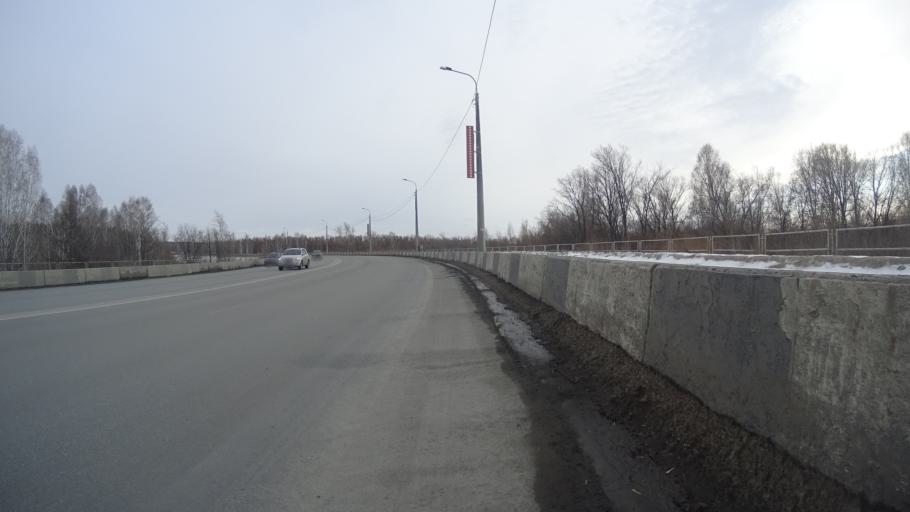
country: RU
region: Chelyabinsk
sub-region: Gorod Chelyabinsk
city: Chelyabinsk
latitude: 55.1500
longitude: 61.3192
